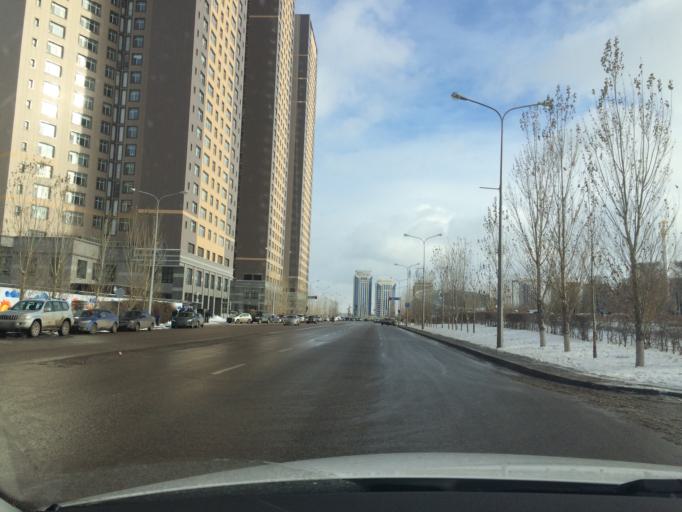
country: KZ
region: Astana Qalasy
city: Astana
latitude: 51.1259
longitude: 71.4645
